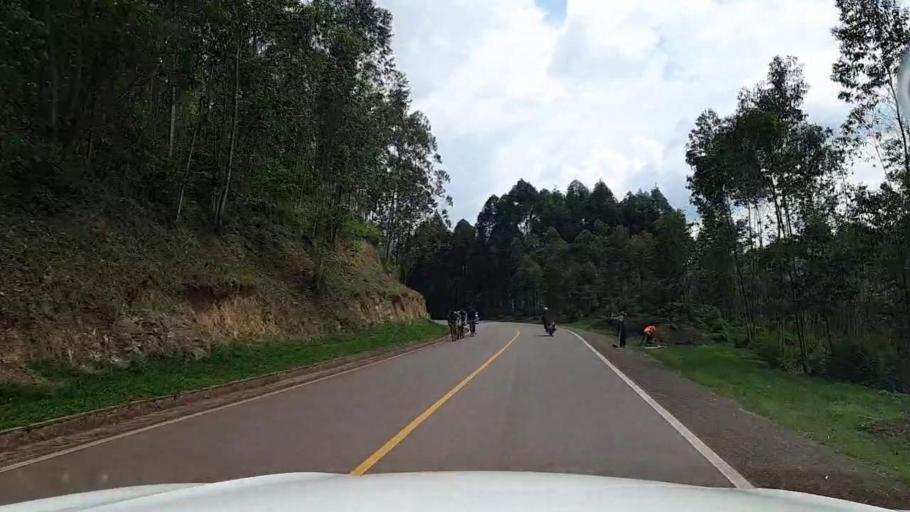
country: RW
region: Kigali
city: Kigali
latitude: -1.8198
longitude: 30.0876
